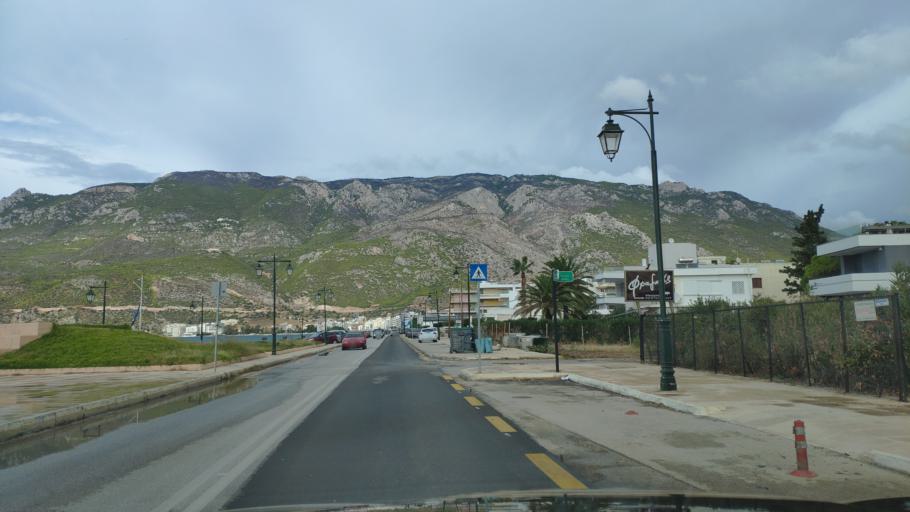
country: GR
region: Peloponnese
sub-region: Nomos Korinthias
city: Loutraki
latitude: 37.9648
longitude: 22.9711
